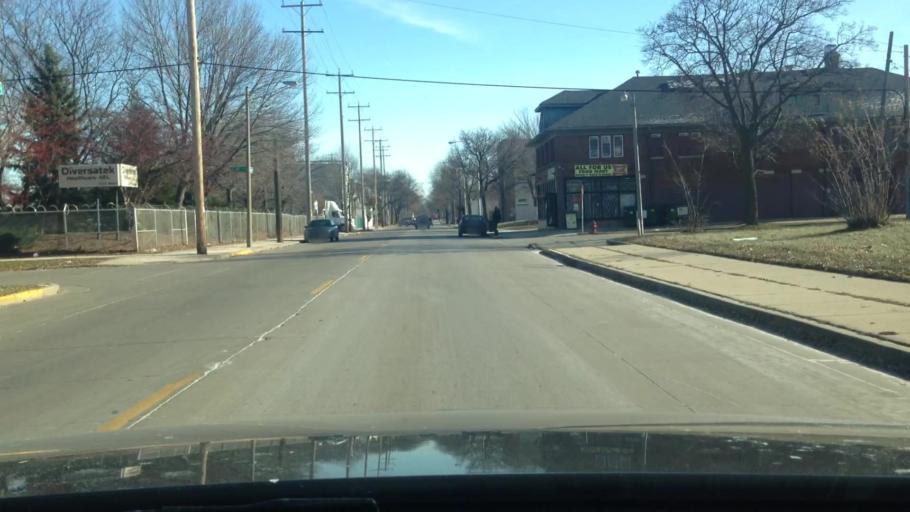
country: US
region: Wisconsin
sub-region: Milwaukee County
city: Shorewood
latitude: 43.0821
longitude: -87.9114
